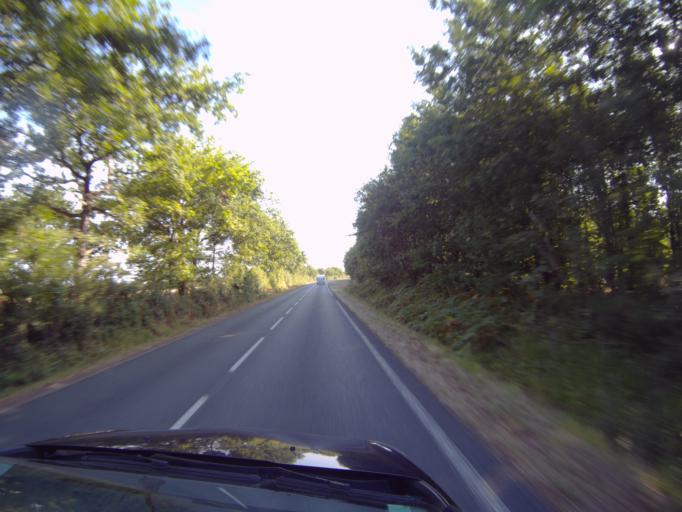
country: FR
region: Pays de la Loire
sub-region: Departement de la Vendee
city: Saint-Hilaire-de-Talmont
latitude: 46.4946
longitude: -1.5836
